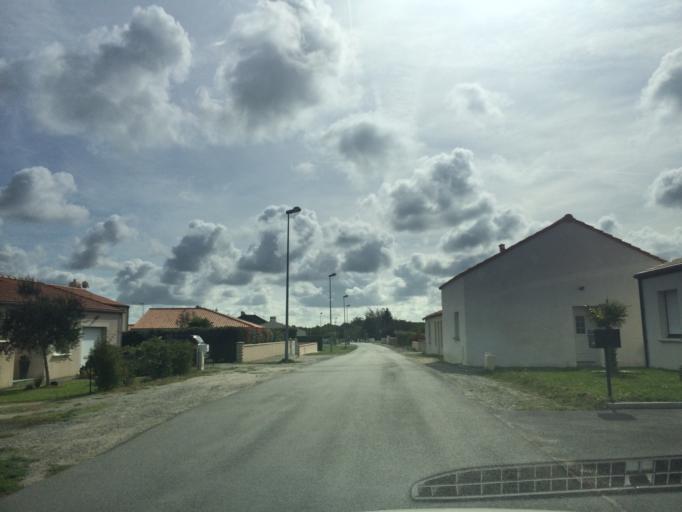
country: FR
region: Pays de la Loire
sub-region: Departement de la Loire-Atlantique
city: Chemere
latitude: 47.1157
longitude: -1.9224
